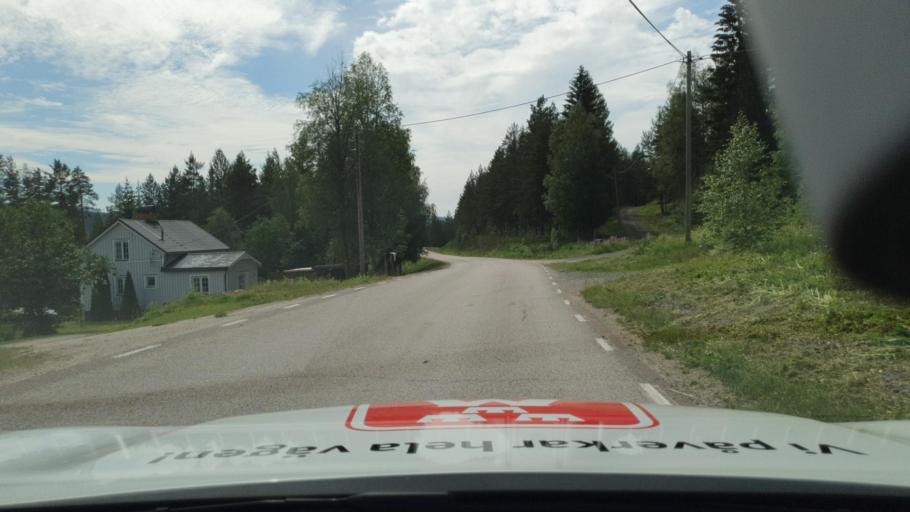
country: NO
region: Hedmark
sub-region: Asnes
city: Flisa
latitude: 60.6935
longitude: 12.4654
